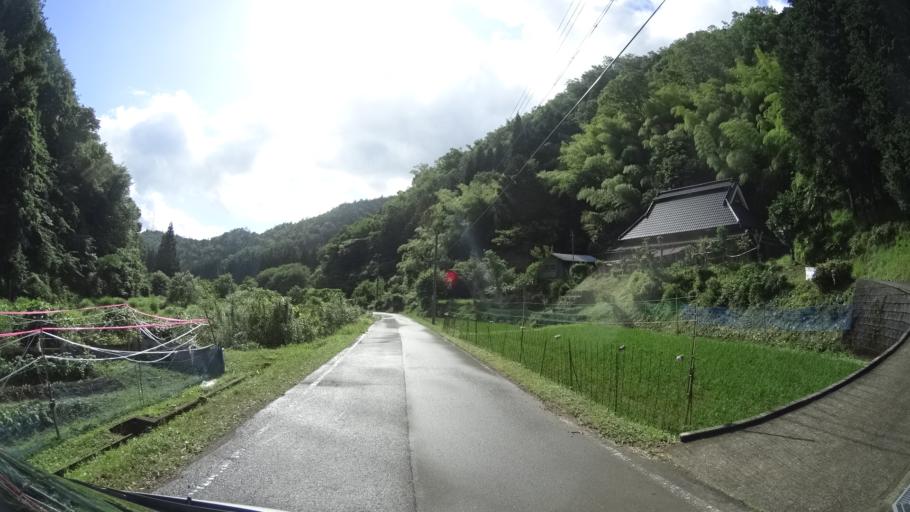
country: JP
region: Kyoto
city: Maizuru
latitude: 35.3939
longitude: 135.2651
